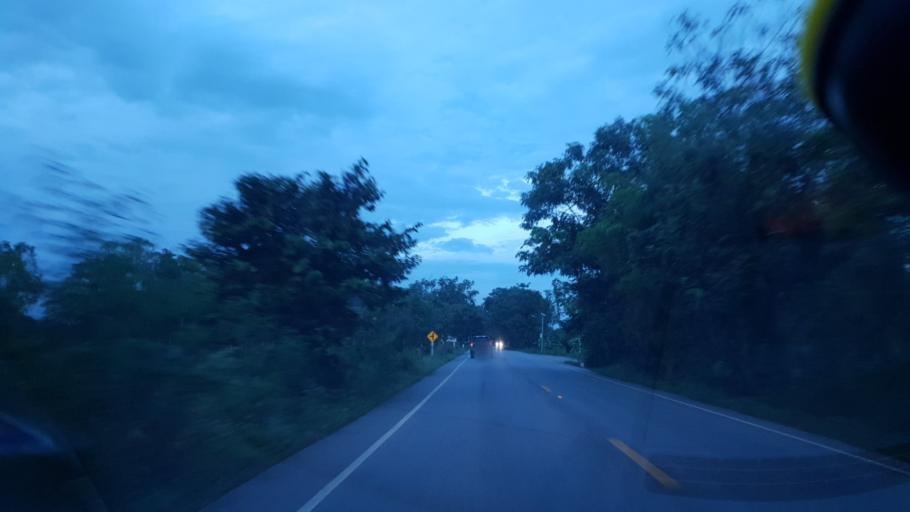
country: TH
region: Chiang Rai
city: Wiang Chai
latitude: 19.9682
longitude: 99.9647
